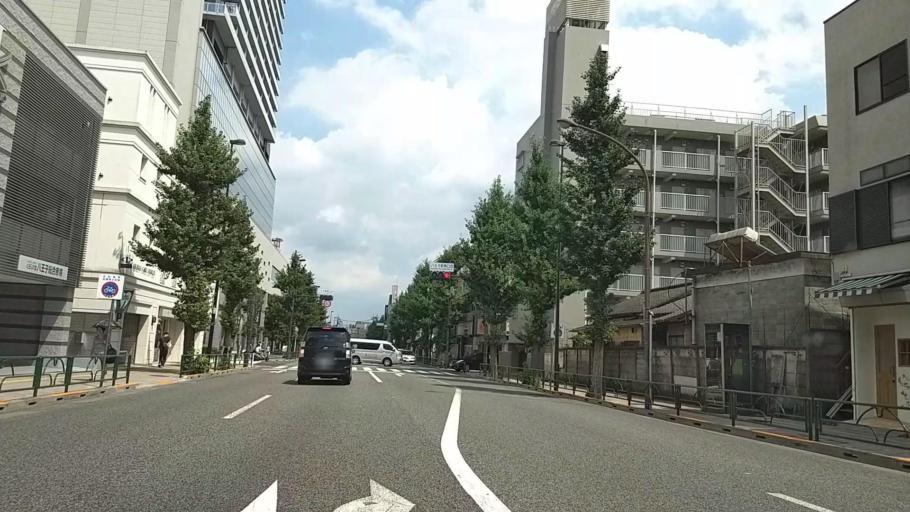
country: JP
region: Tokyo
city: Hachioji
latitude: 35.6542
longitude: 139.3363
